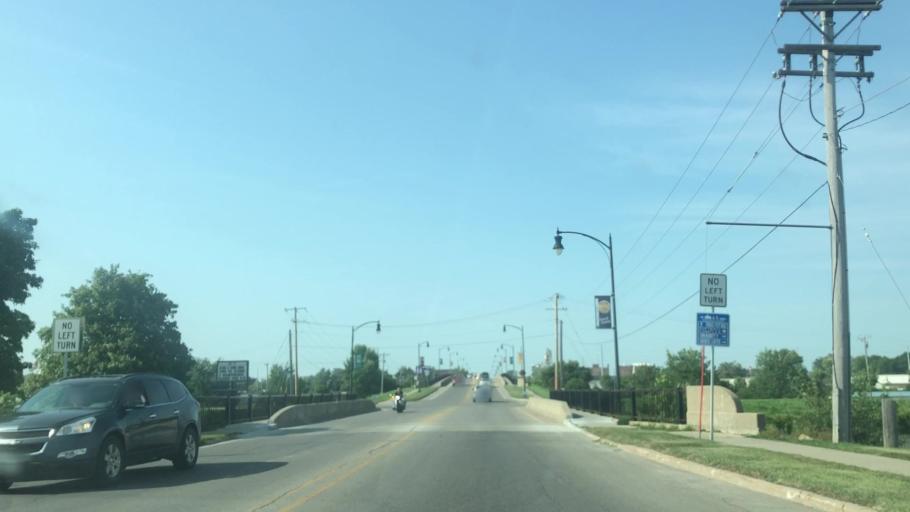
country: US
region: Iowa
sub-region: Marshall County
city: Marshalltown
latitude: 42.0393
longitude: -92.9128
